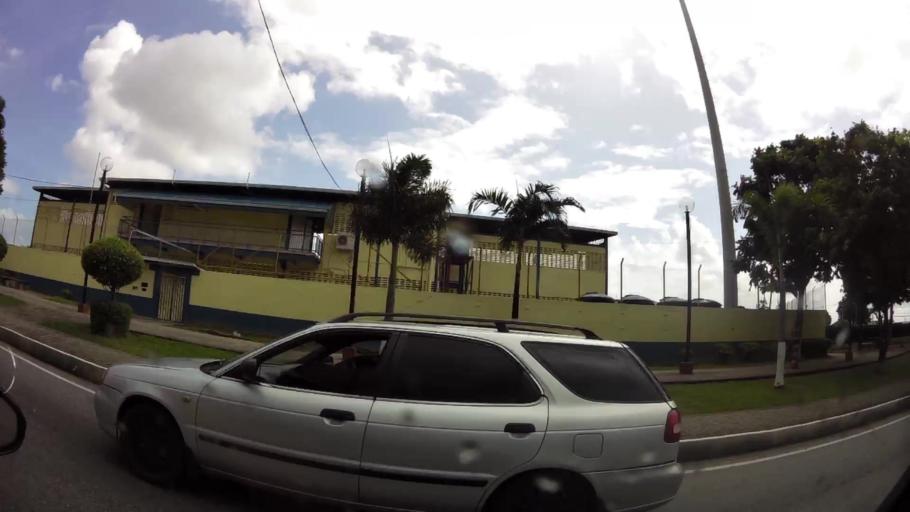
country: TT
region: Borough of Arima
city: Arima
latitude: 10.6376
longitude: -61.2848
